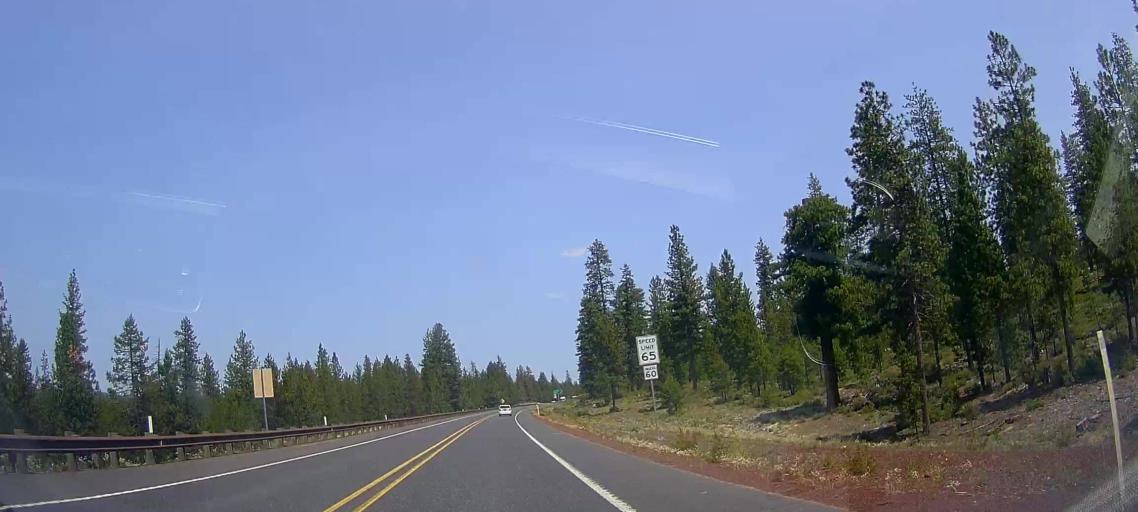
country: US
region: Oregon
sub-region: Deschutes County
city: La Pine
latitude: 43.4836
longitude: -121.6854
